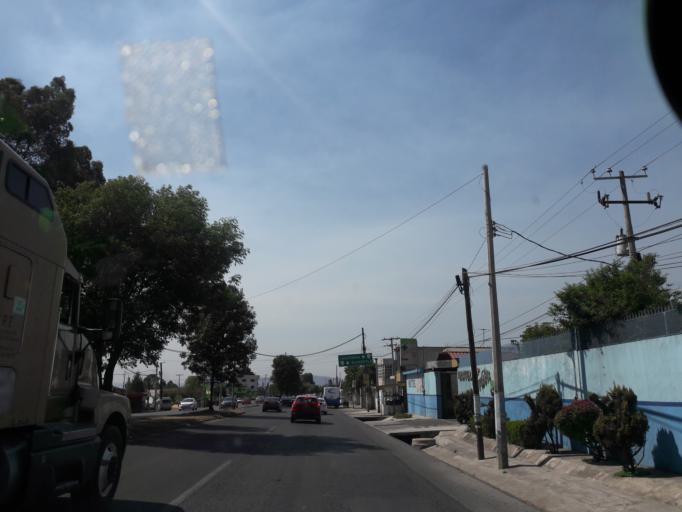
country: MX
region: Tlaxcala
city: Xiloxoxtla
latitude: 19.2618
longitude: -98.1998
